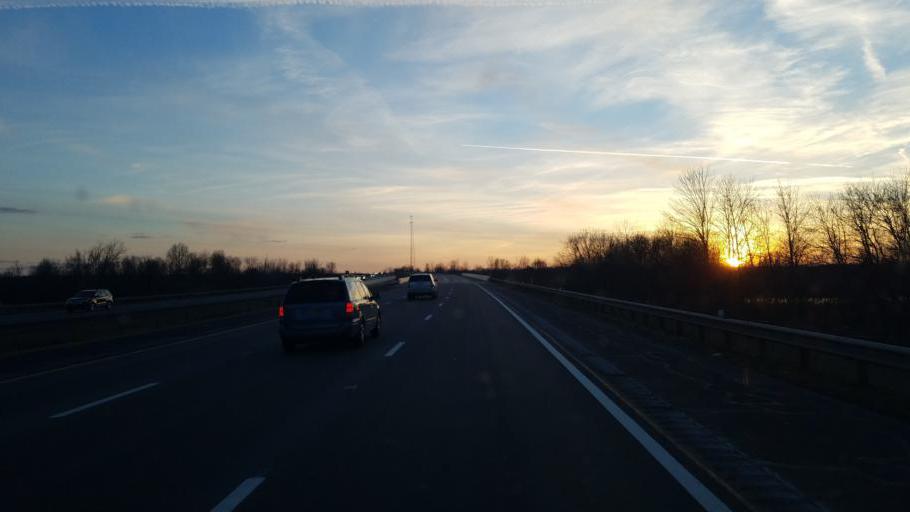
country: US
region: Ohio
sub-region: Medina County
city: Lodi
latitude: 40.9945
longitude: -82.0220
